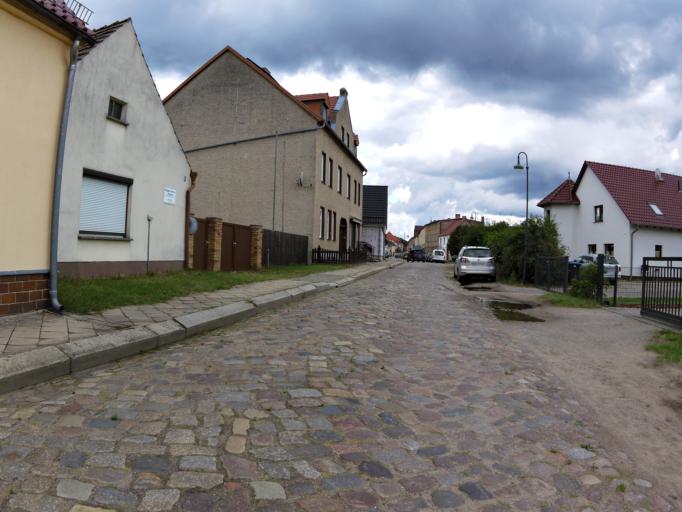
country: DE
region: Brandenburg
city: Storkow
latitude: 52.2542
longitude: 13.9235
